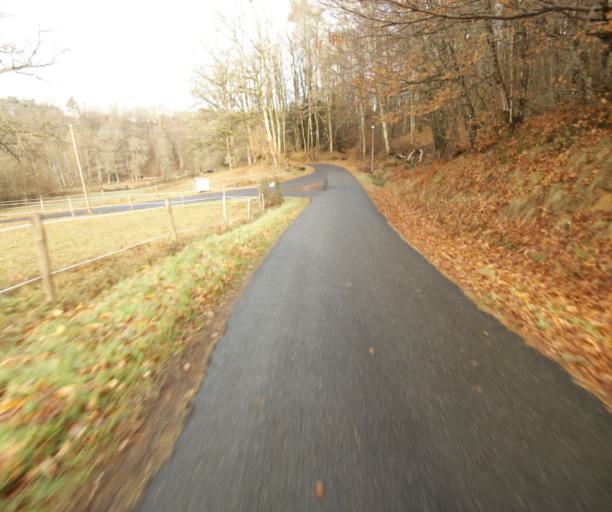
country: FR
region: Limousin
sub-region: Departement de la Correze
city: Saint-Mexant
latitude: 45.2538
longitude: 1.6441
